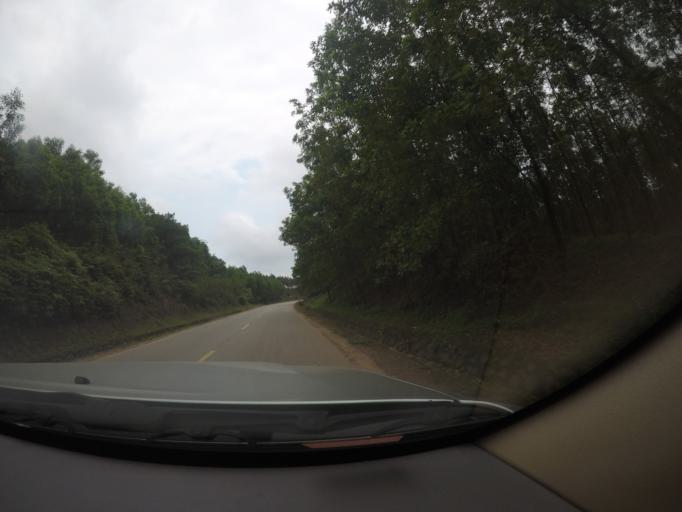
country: VN
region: Quang Binh
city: Kien Giang
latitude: 17.1357
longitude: 106.7730
